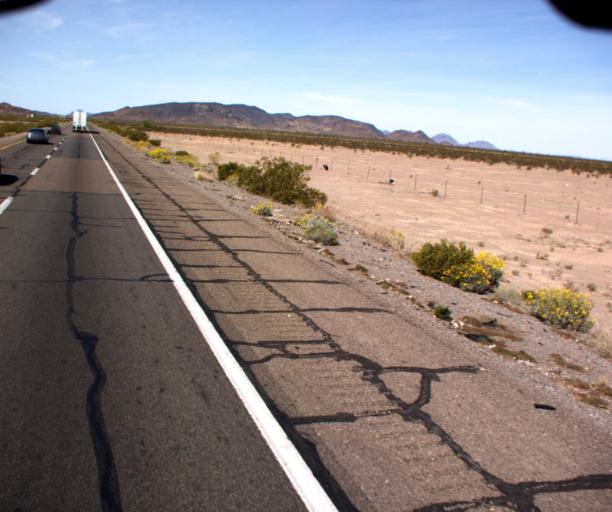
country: US
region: Arizona
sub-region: La Paz County
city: Salome
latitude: 33.6411
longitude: -113.8375
